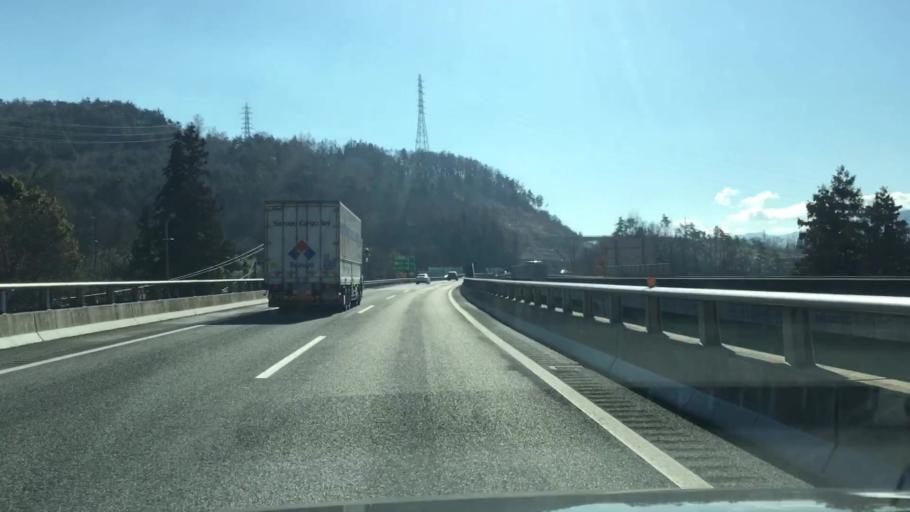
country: JP
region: Nagano
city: Ueda
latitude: 36.4712
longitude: 138.1978
